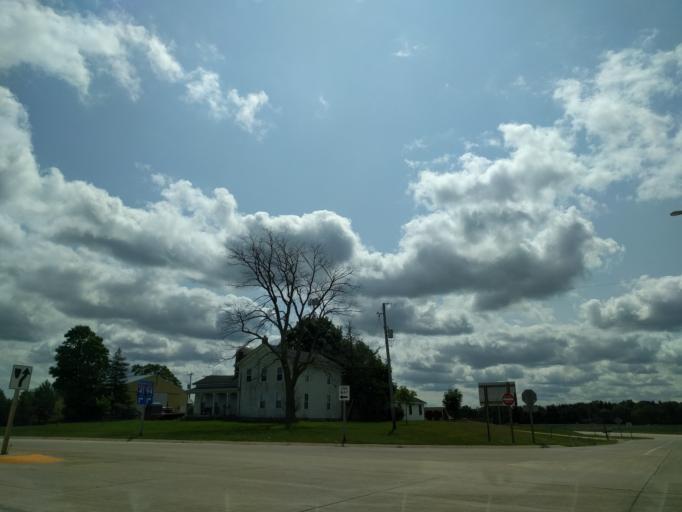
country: US
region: Wisconsin
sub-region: Racine County
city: Caledonia
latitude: 42.8079
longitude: -87.9562
